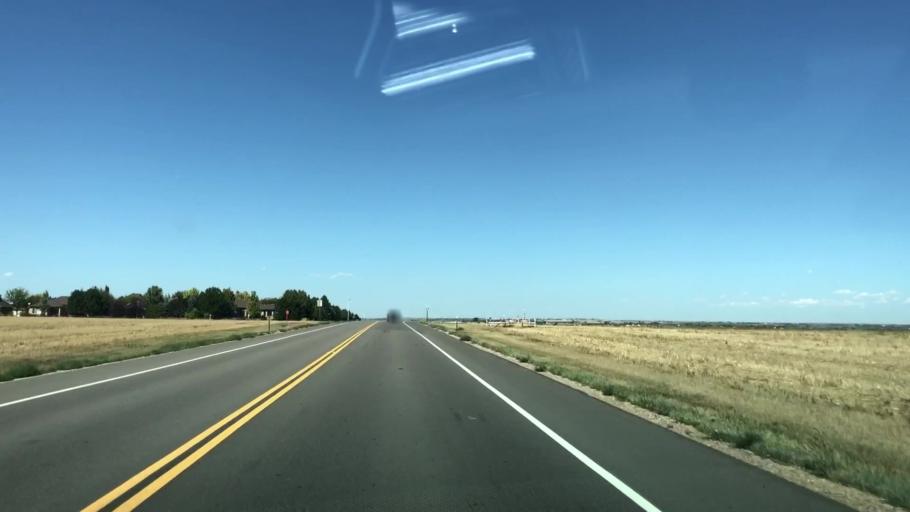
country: US
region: Colorado
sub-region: Weld County
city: Windsor
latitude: 40.4590
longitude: -104.9441
